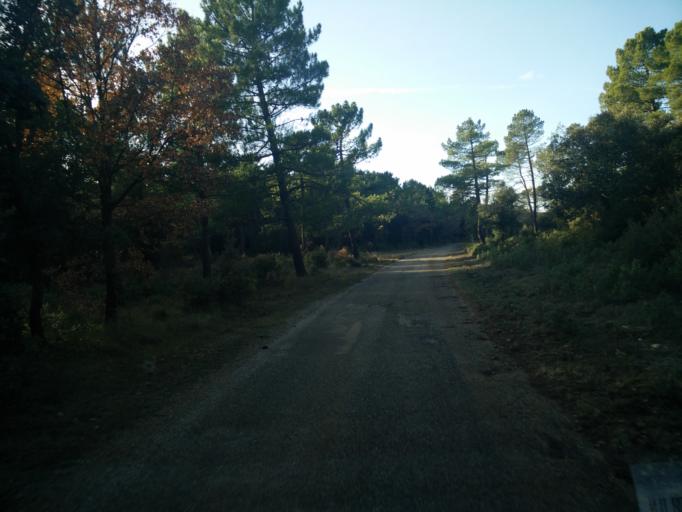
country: FR
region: Provence-Alpes-Cote d'Azur
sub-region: Departement du Var
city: Signes
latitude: 43.2385
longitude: 5.8791
